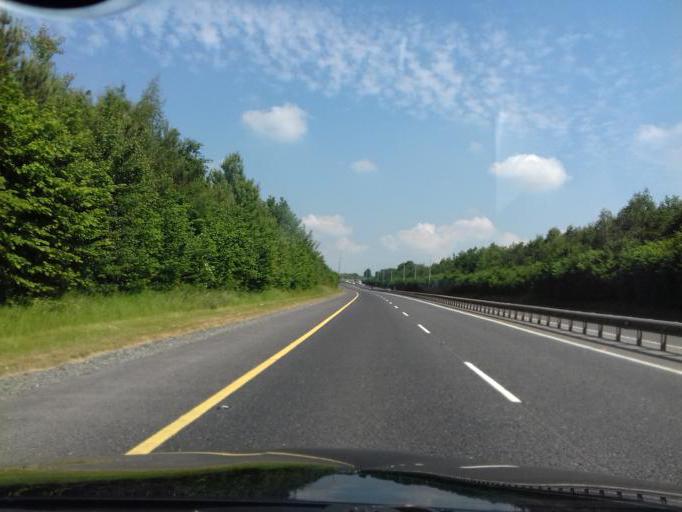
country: IE
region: Leinster
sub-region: An Mhi
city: Ashbourne
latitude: 53.5181
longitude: -6.4197
